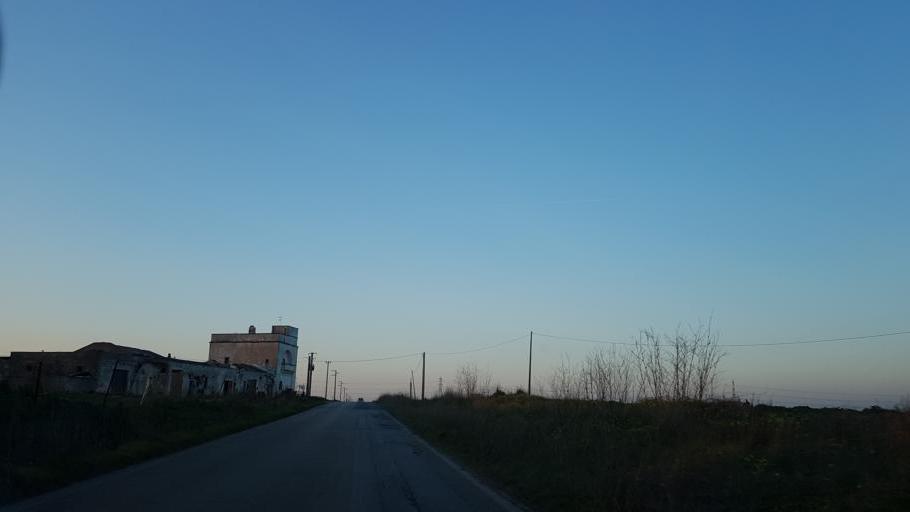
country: IT
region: Apulia
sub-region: Provincia di Brindisi
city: La Rosa
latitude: 40.5825
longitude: 17.9484
